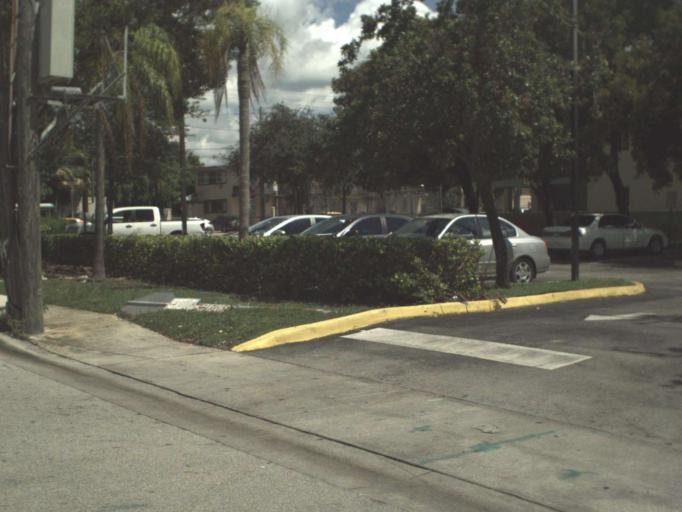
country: US
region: Florida
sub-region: Miami-Dade County
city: Miami
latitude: 25.7664
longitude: -80.2074
